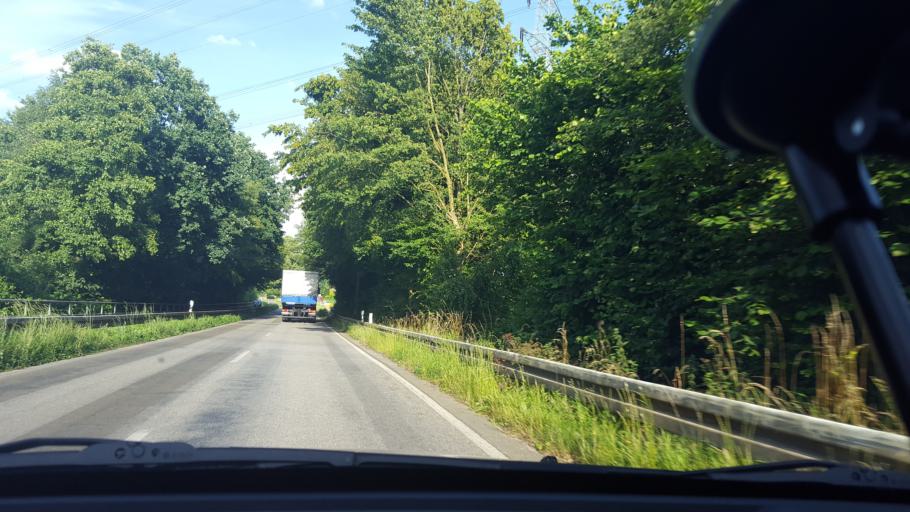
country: DE
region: North Rhine-Westphalia
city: Marl
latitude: 51.6581
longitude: 7.0550
